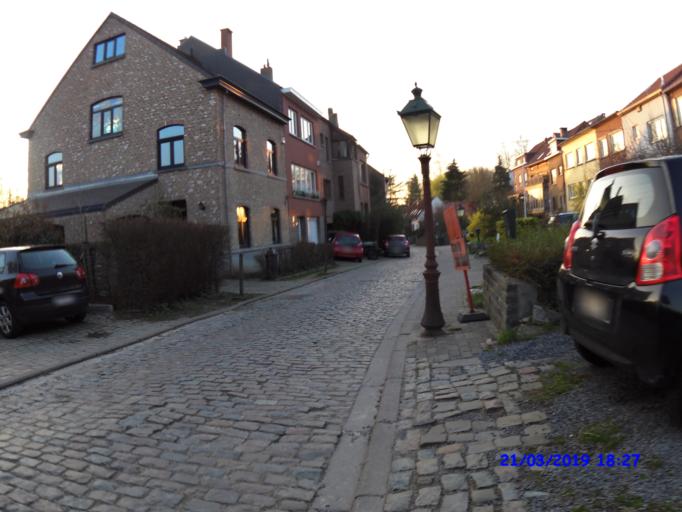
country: BE
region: Flanders
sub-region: Provincie Vlaams-Brabant
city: Linkebeek
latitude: 50.7795
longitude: 4.3285
